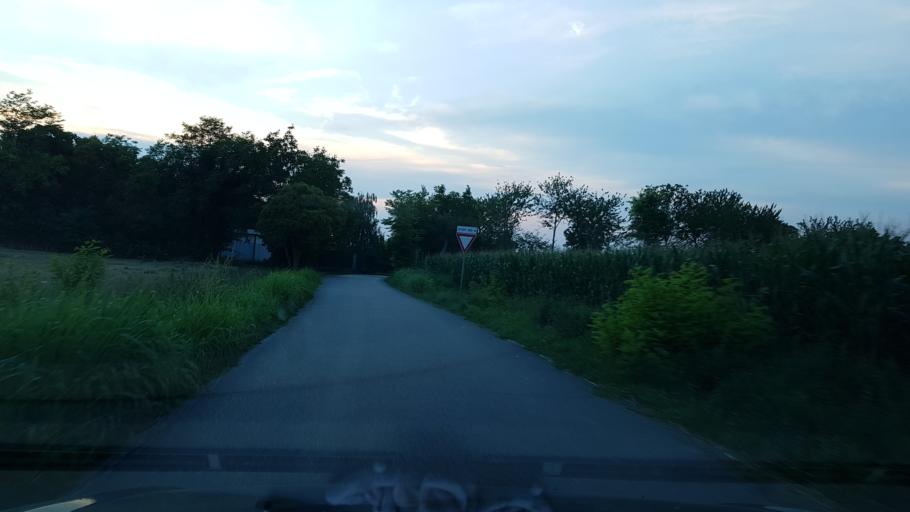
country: IT
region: Friuli Venezia Giulia
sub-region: Provincia di Gorizia
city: San Pier d'Isonzo
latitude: 45.8395
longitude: 13.4562
